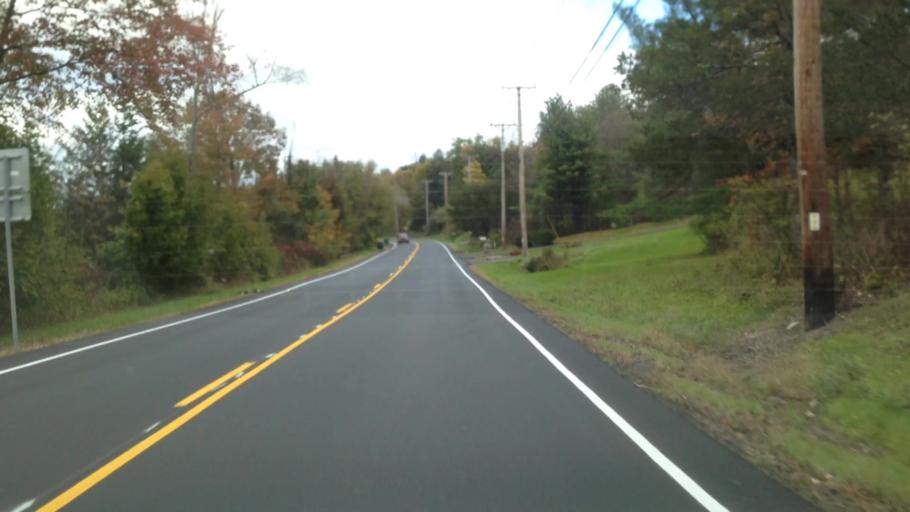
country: US
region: New York
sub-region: Ulster County
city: New Paltz
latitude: 41.7331
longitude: -74.0936
